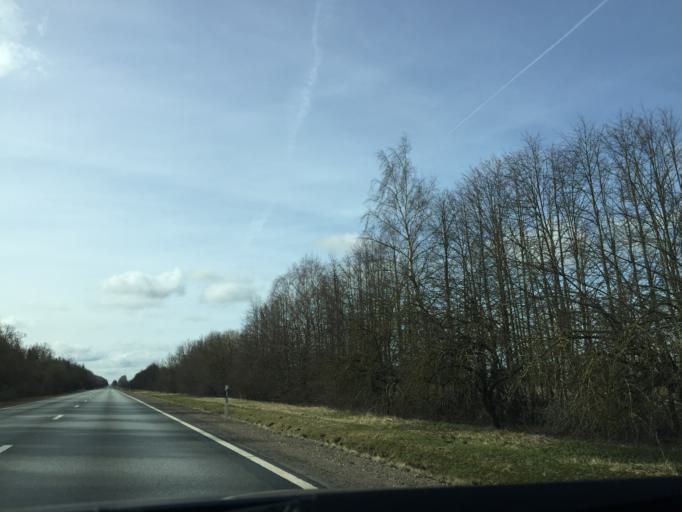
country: LV
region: Jelgava
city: Jelgava
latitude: 56.5228
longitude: 23.7043
